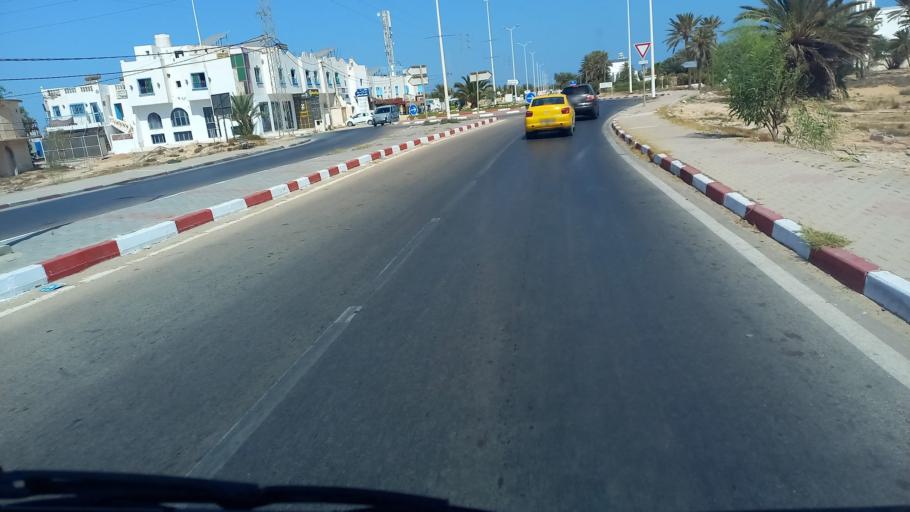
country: TN
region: Madanin
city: Midoun
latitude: 33.8637
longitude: 10.9627
